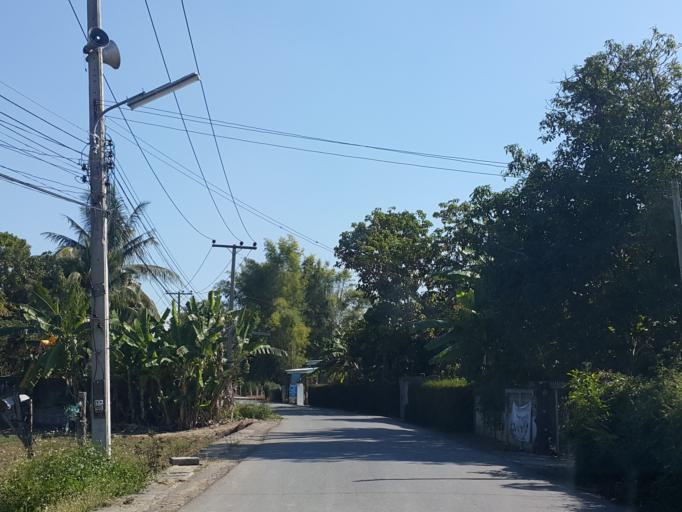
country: TH
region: Chiang Mai
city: San Sai
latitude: 18.8867
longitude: 98.9896
